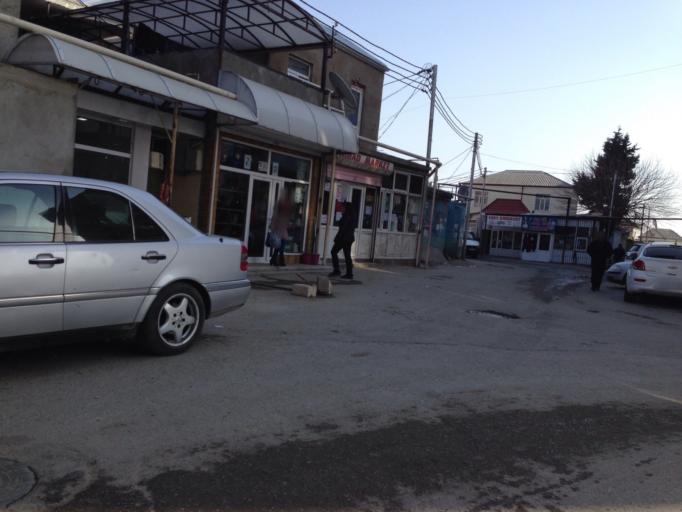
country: AZ
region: Baki
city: Baku
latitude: 40.3971
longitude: 49.8798
